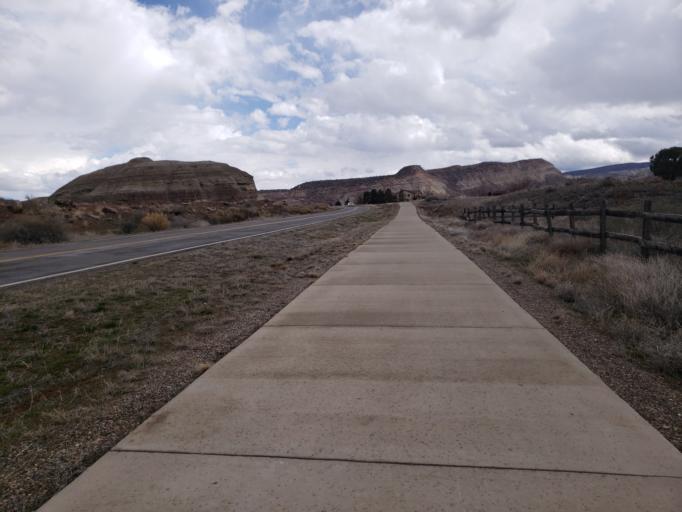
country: US
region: Colorado
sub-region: Mesa County
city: Redlands
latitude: 39.0461
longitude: -108.6345
